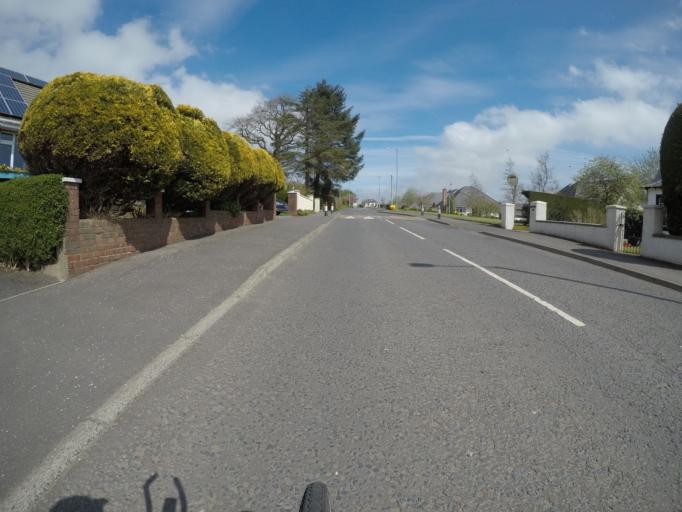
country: GB
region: Scotland
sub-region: East Ayrshire
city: Stewarton
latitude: 55.6869
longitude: -4.5022
